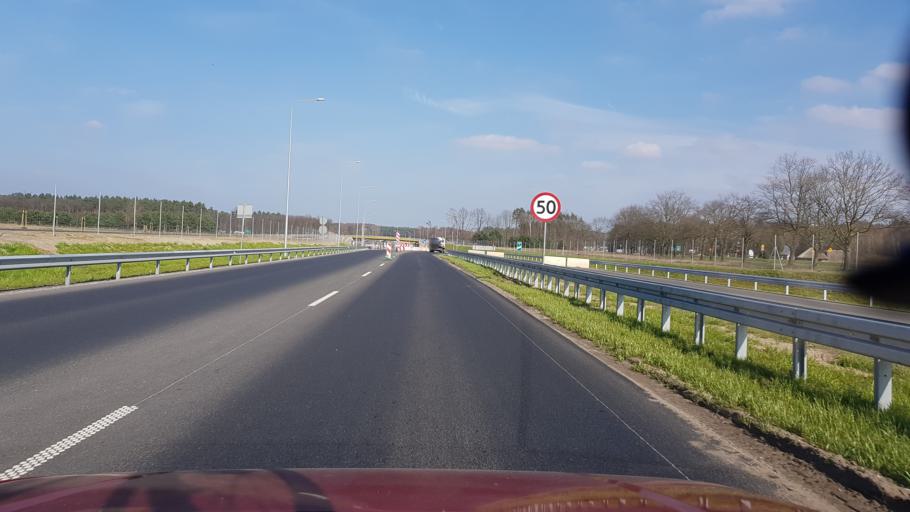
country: PL
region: West Pomeranian Voivodeship
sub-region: Powiat goleniowski
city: Osina
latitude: 53.6291
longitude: 14.9894
